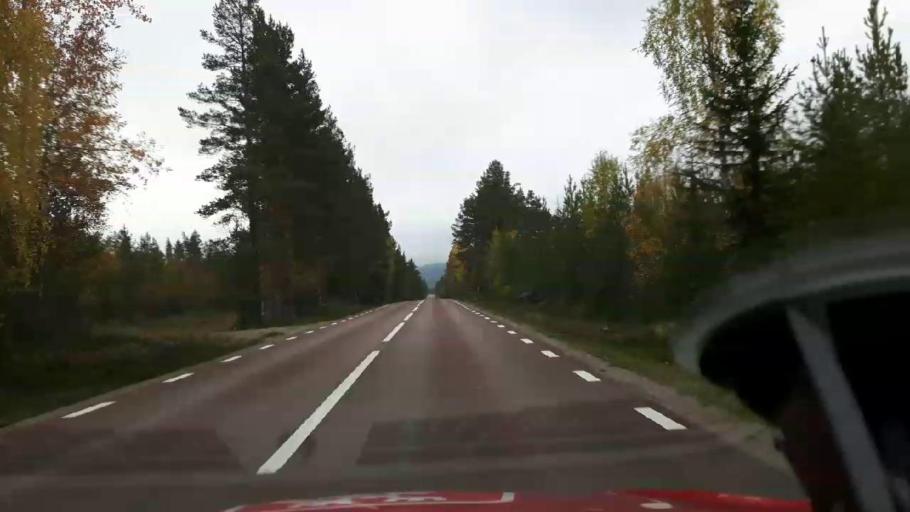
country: SE
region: Jaemtland
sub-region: Harjedalens Kommun
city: Sveg
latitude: 62.3259
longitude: 14.7407
